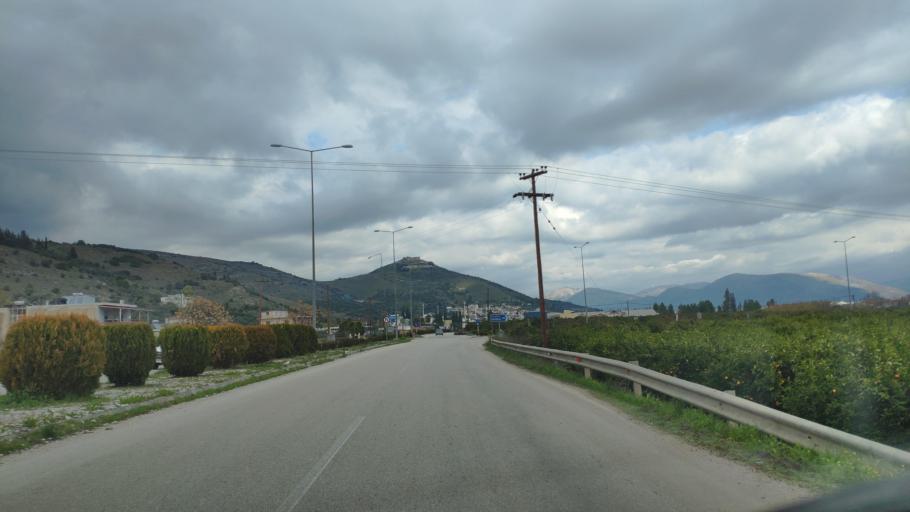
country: GR
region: Peloponnese
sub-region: Nomos Argolidos
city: Argos
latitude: 37.6152
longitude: 22.7115
